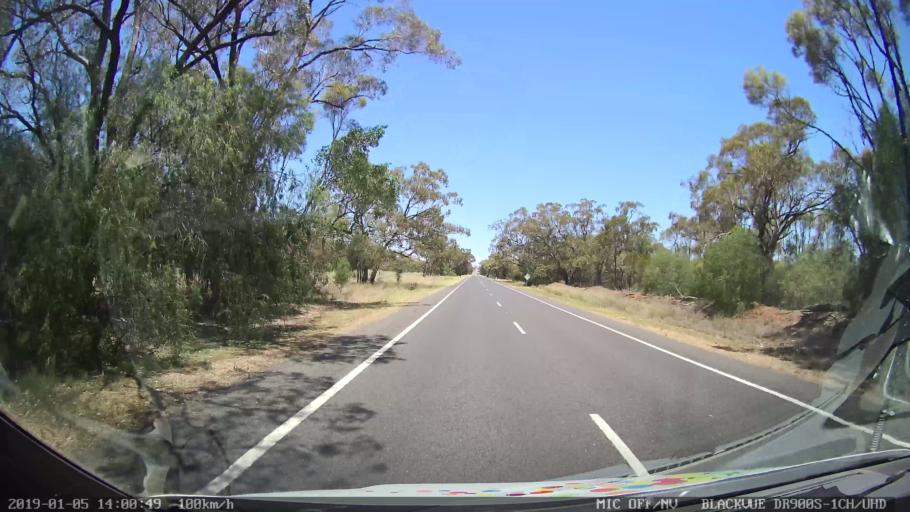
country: AU
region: New South Wales
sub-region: Gunnedah
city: Gunnedah
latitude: -31.1635
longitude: 150.3172
